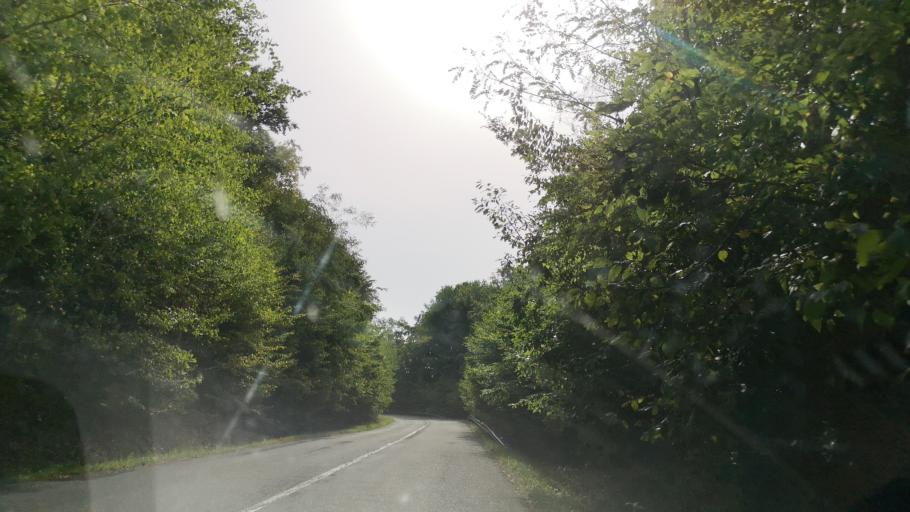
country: SK
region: Banskobystricky
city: Revuca
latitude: 48.5860
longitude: 20.0579
